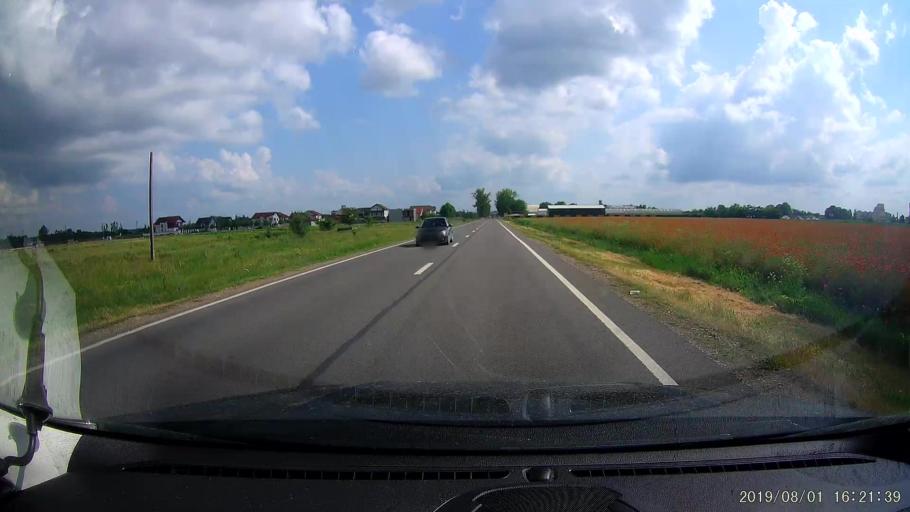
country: RO
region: Calarasi
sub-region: Municipiul Calarasi
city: Calarasi
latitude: 44.2140
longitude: 27.3395
